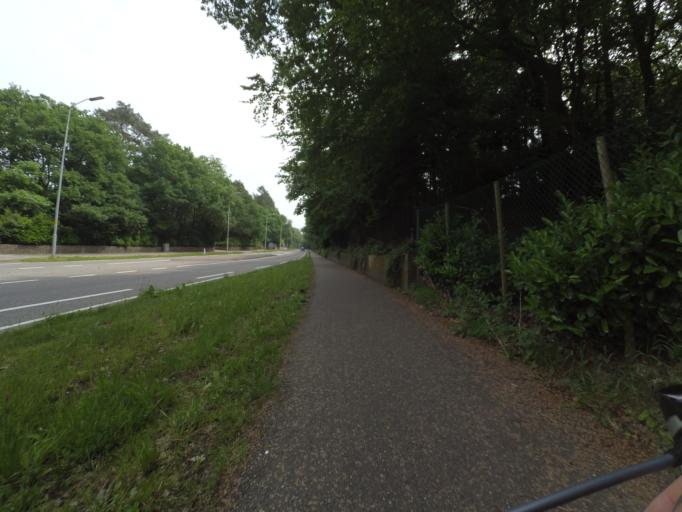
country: NL
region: Gelderland
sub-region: Gemeente Renkum
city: Heelsum
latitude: 51.9808
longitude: 5.7670
